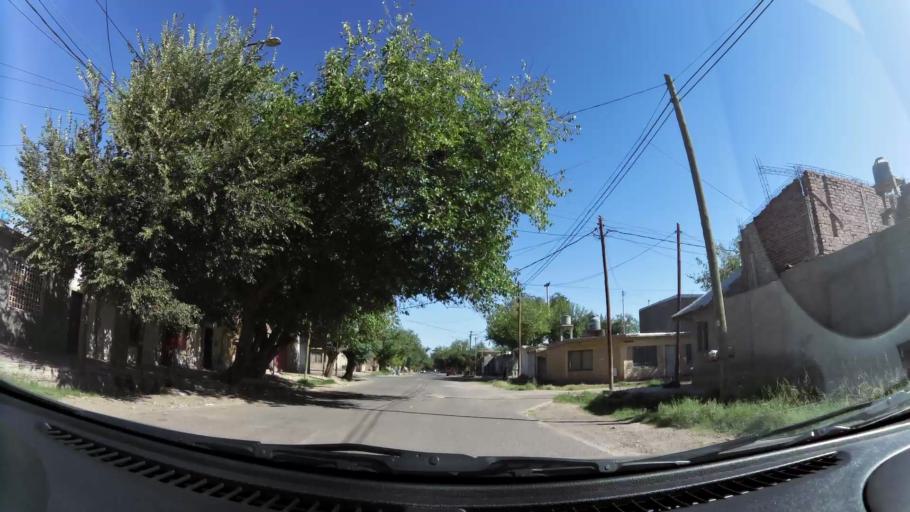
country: AR
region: Mendoza
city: Mendoza
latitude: -32.8812
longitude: -68.8044
